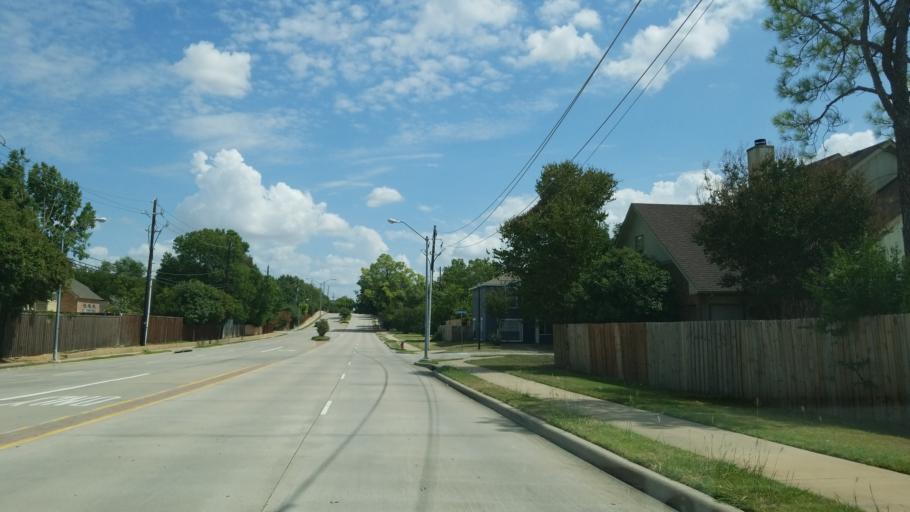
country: US
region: Texas
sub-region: Tarrant County
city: Euless
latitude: 32.8811
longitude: -97.0949
